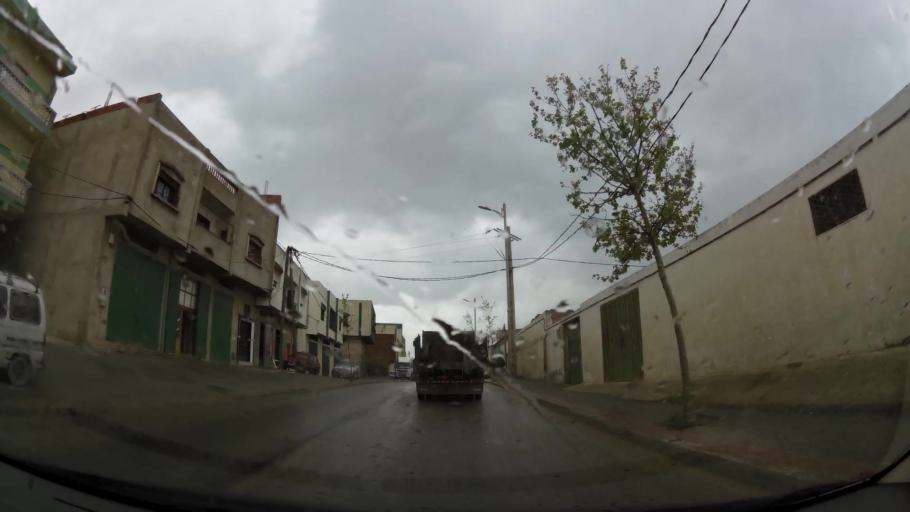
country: MA
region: Tanger-Tetouan
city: Tetouan
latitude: 35.5577
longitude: -5.4072
